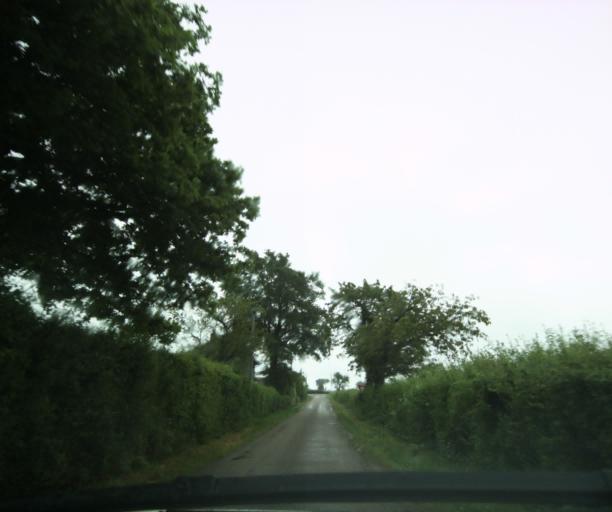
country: FR
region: Bourgogne
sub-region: Departement de Saone-et-Loire
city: Charolles
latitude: 46.3626
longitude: 4.2583
